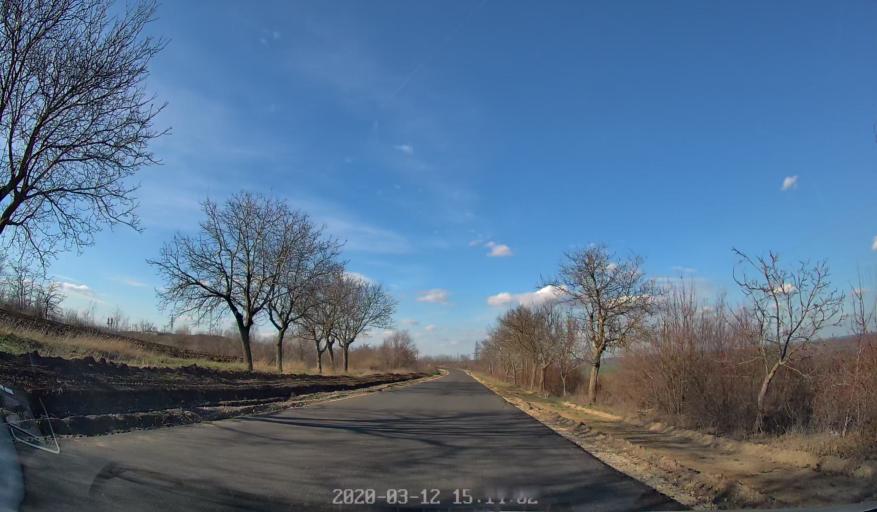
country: MD
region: Chisinau
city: Ciorescu
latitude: 47.2323
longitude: 28.9554
